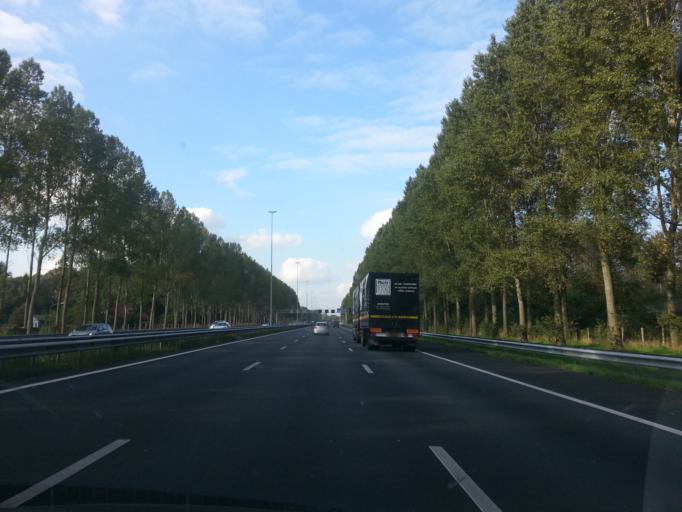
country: NL
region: North Brabant
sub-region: Gemeente Best
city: Best
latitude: 51.5488
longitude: 5.3676
